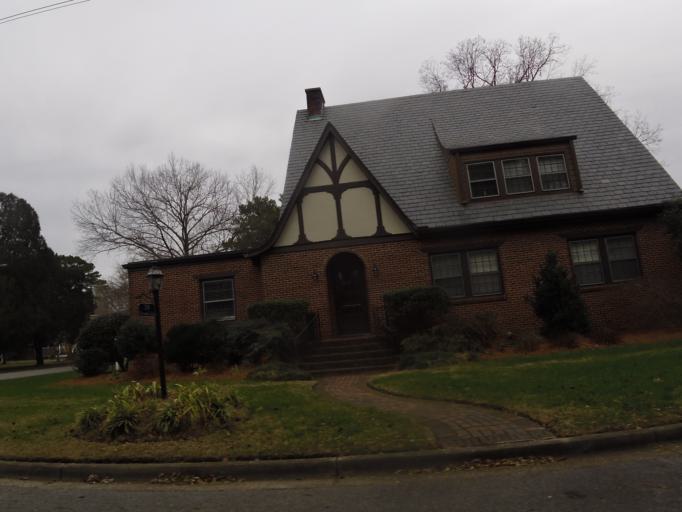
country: US
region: Virginia
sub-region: City of Portsmouth
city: Portsmouth Heights
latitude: 36.8407
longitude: -76.3546
